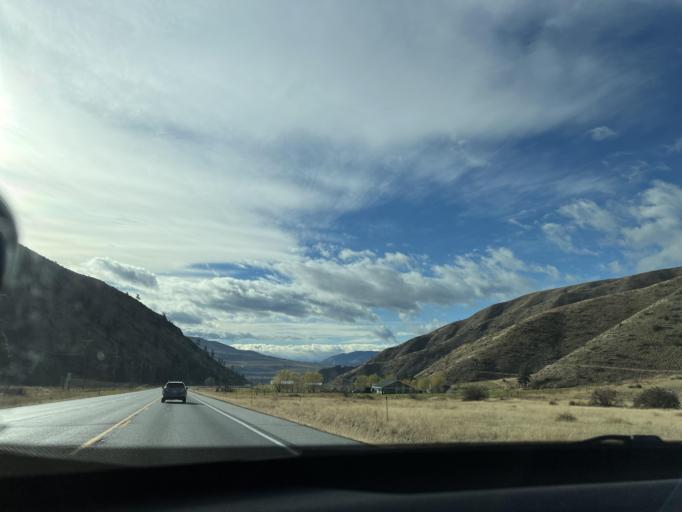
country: US
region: Washington
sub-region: Chelan County
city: Manson
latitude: 47.7939
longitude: -120.1338
